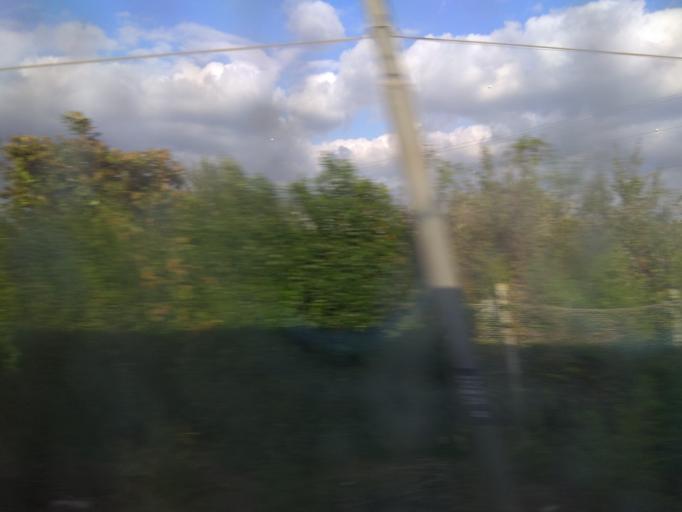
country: IT
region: Latium
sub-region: Citta metropolitana di Roma Capitale
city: Maccarese
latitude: 41.8725
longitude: 12.2439
